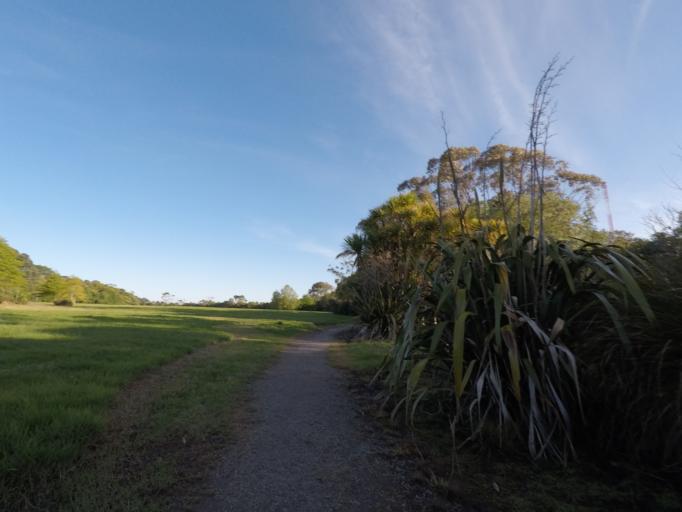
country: NZ
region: Auckland
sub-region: Auckland
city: Rosebank
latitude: -36.8409
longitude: 174.6326
